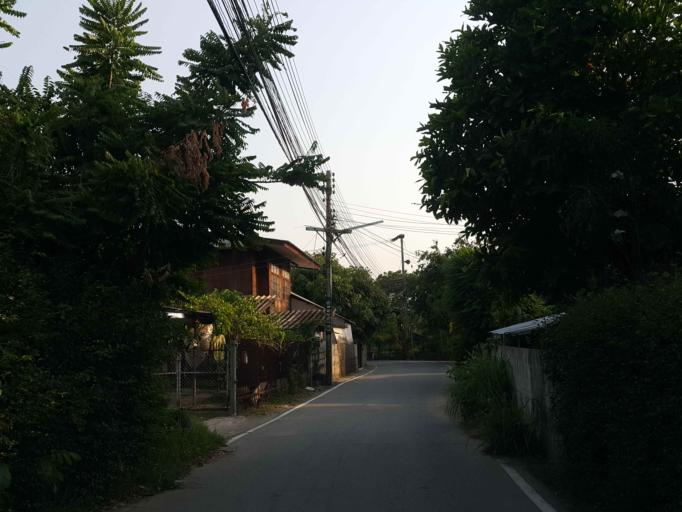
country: TH
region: Chiang Mai
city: San Kamphaeng
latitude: 18.7725
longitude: 99.0755
